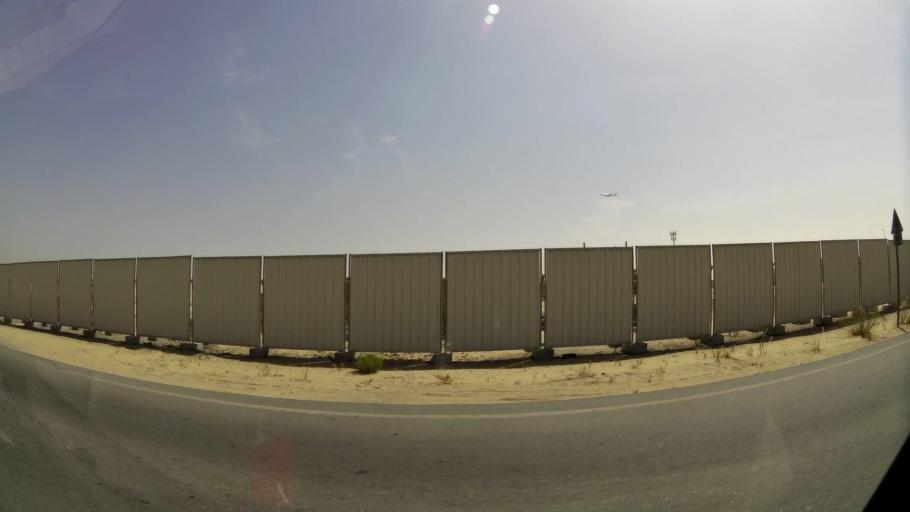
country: AE
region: Ash Shariqah
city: Sharjah
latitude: 25.1973
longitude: 55.4368
